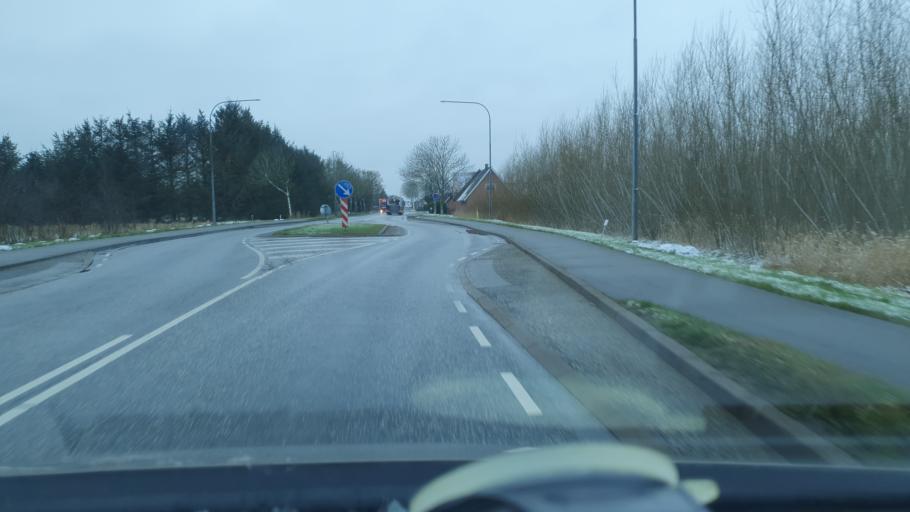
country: DK
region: North Denmark
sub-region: Jammerbugt Kommune
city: Brovst
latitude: 57.1128
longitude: 9.5978
